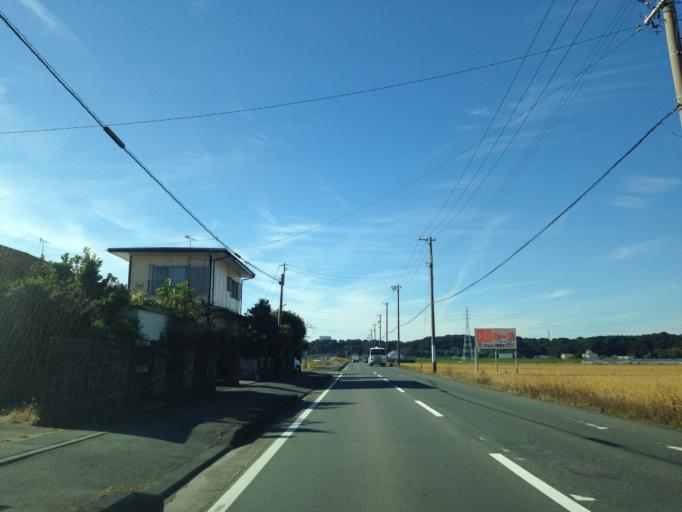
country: JP
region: Shizuoka
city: Fukuroi
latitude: 34.7349
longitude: 137.8995
